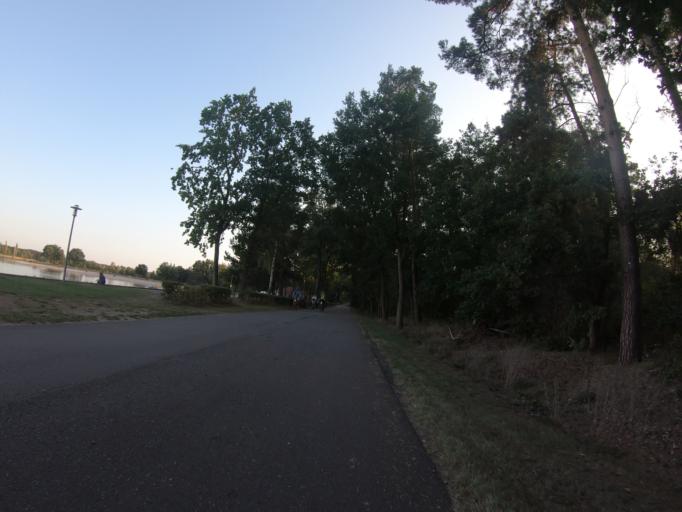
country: DE
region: Lower Saxony
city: Calberlah
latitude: 52.4547
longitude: 10.6176
